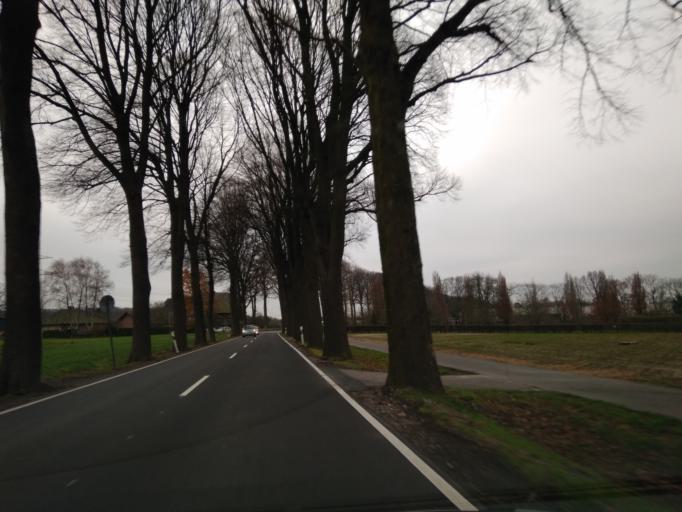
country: DE
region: North Rhine-Westphalia
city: Marl
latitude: 51.6216
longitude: 7.0758
